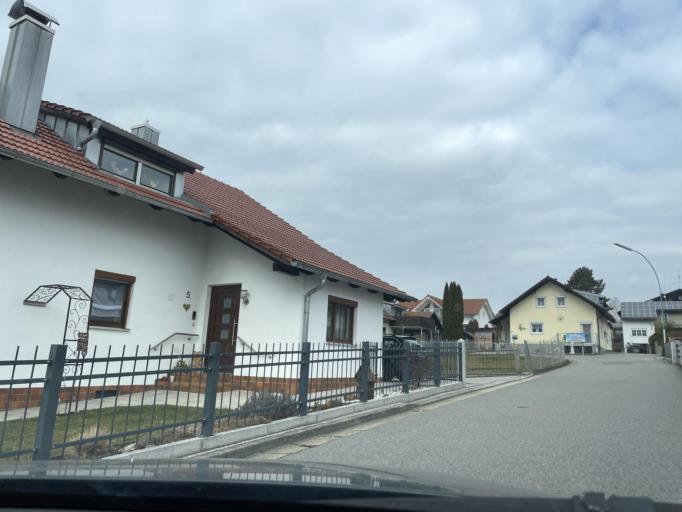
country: DE
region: Bavaria
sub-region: Lower Bavaria
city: Viechtach
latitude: 49.0812
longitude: 12.8753
